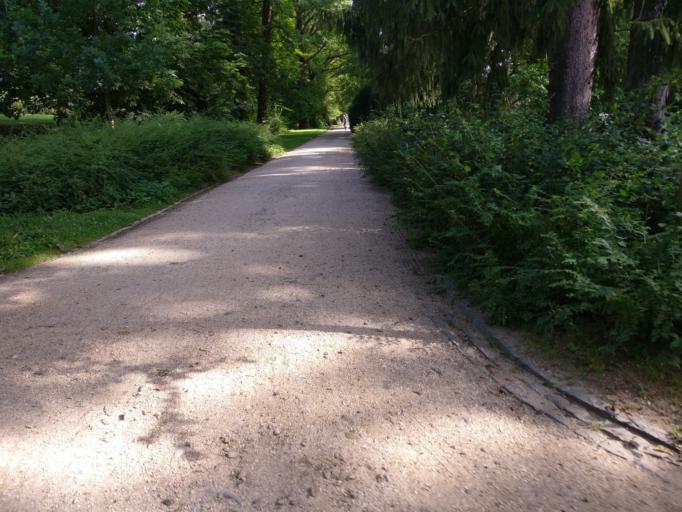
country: DE
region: Hesse
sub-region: Regierungsbezirk Darmstadt
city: Bad Homburg vor der Hoehe
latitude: 50.2282
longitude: 8.6076
